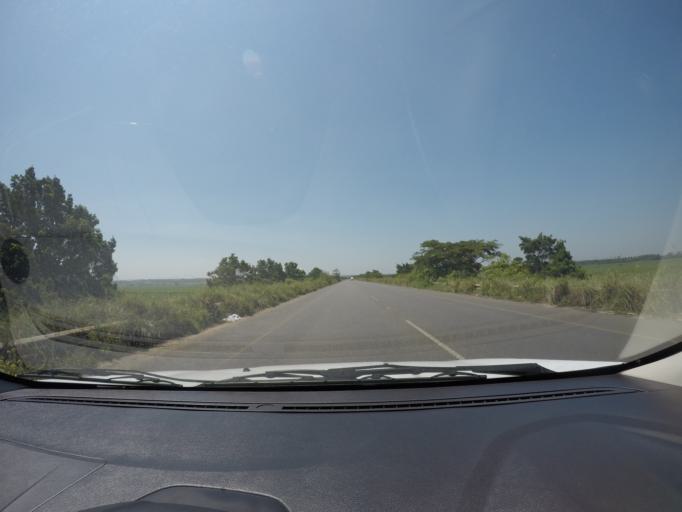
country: ZA
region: KwaZulu-Natal
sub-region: uThungulu District Municipality
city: Empangeni
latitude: -28.7891
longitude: 31.9581
